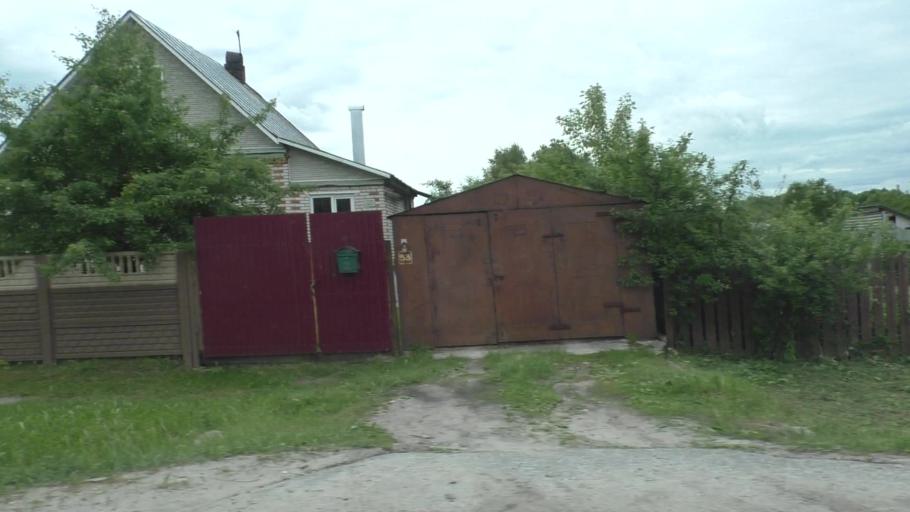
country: RU
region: Moskovskaya
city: Il'inskiy Pogost
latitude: 55.5030
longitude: 38.7918
